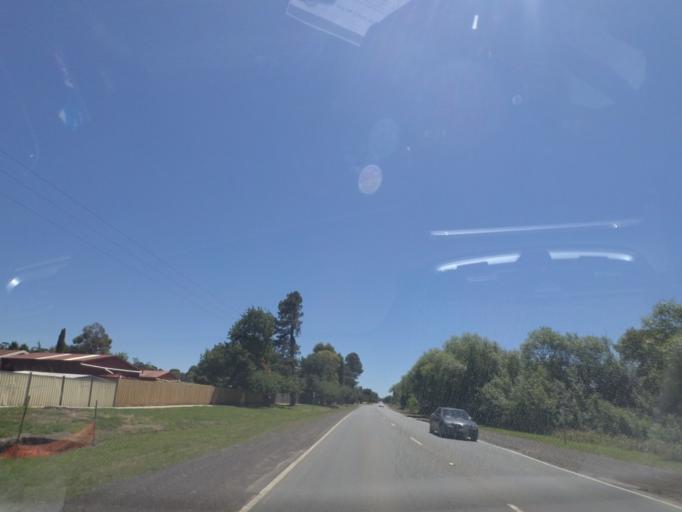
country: AU
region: Victoria
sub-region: Whittlesea
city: Whittlesea
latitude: -37.4176
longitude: 144.9902
